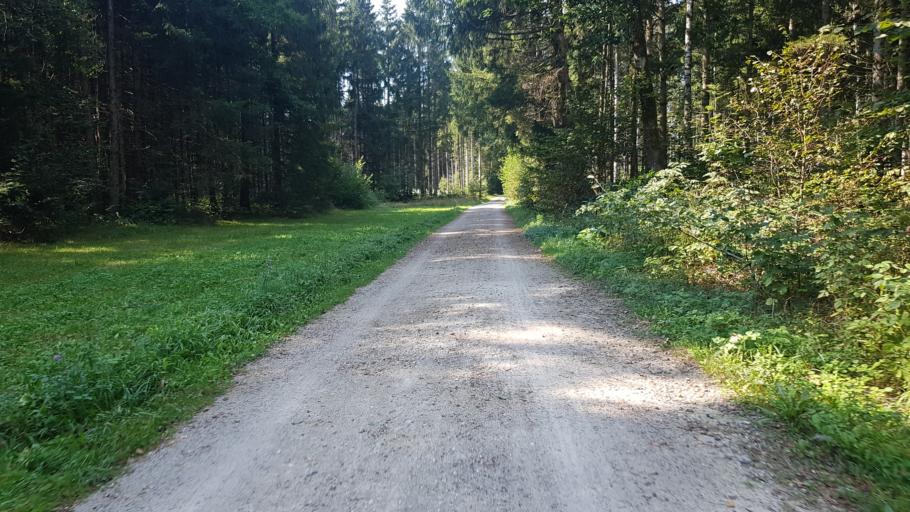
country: DE
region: Bavaria
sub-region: Upper Bavaria
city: Krailling
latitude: 48.0937
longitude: 11.3804
